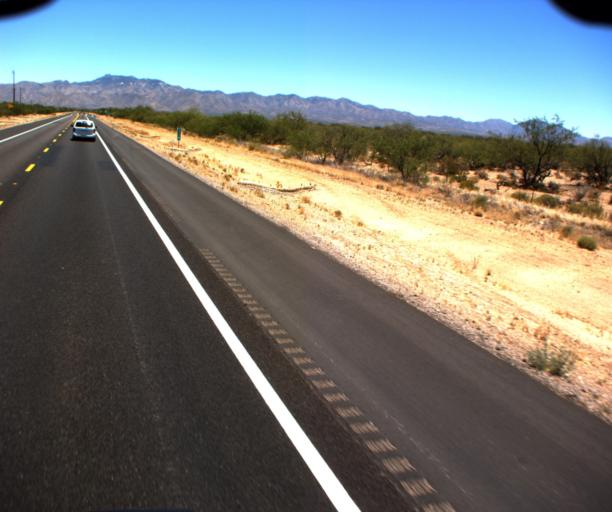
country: US
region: Arizona
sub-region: Pima County
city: Sells
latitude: 31.9266
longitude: -111.7984
